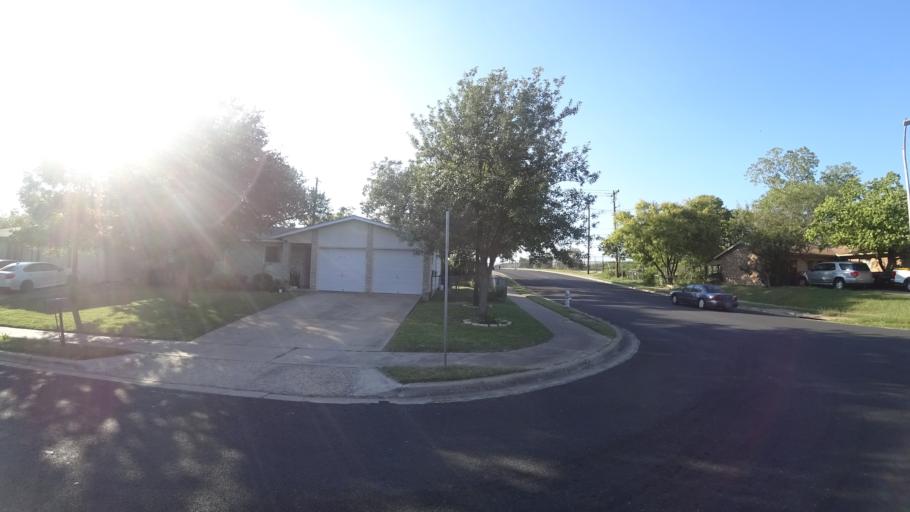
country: US
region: Texas
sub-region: Travis County
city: Wells Branch
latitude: 30.3592
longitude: -97.6825
